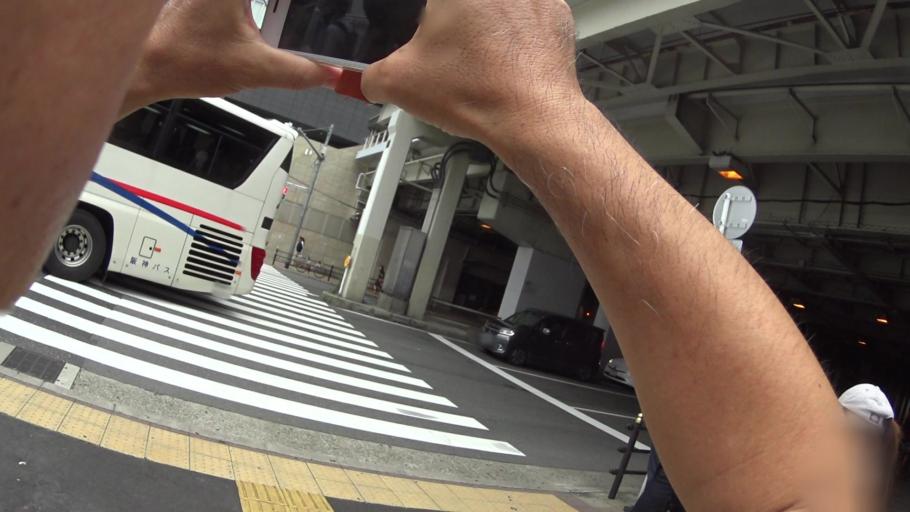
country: JP
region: Osaka
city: Osaka-shi
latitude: 34.7022
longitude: 135.4936
